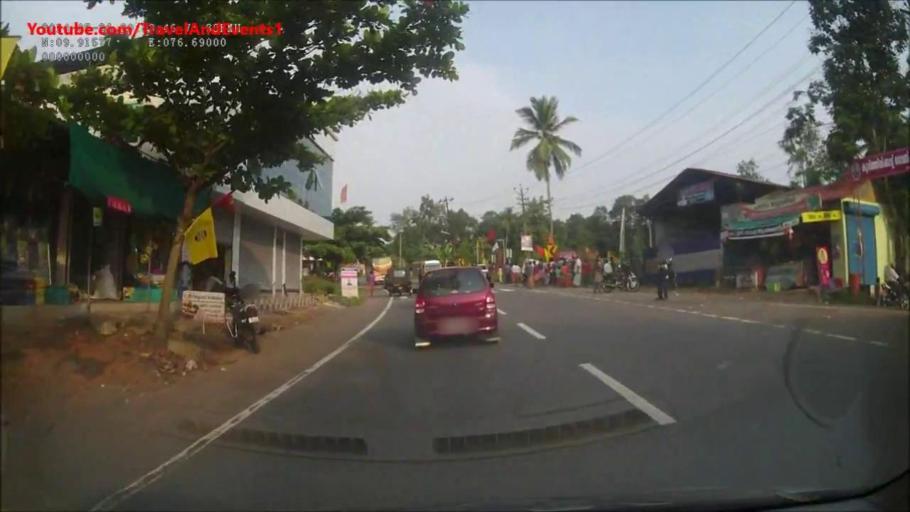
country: IN
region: Kerala
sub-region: Ernakulam
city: Muvattupula
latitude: 9.9165
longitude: 76.6883
